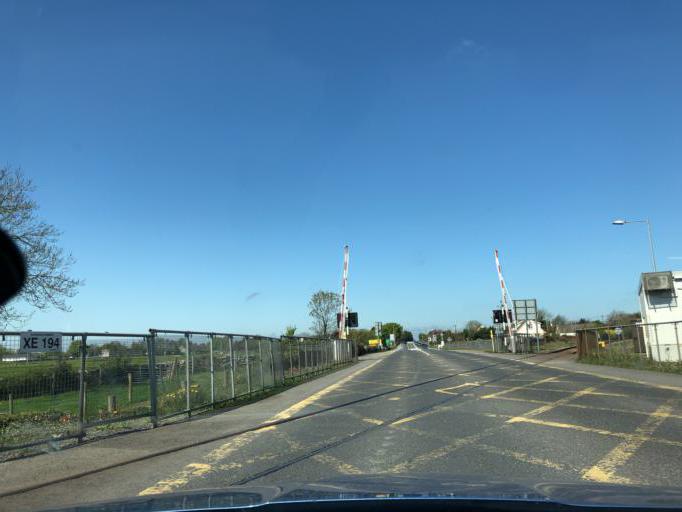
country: IE
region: Connaught
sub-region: County Galway
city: Athenry
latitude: 53.2342
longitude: -8.7420
